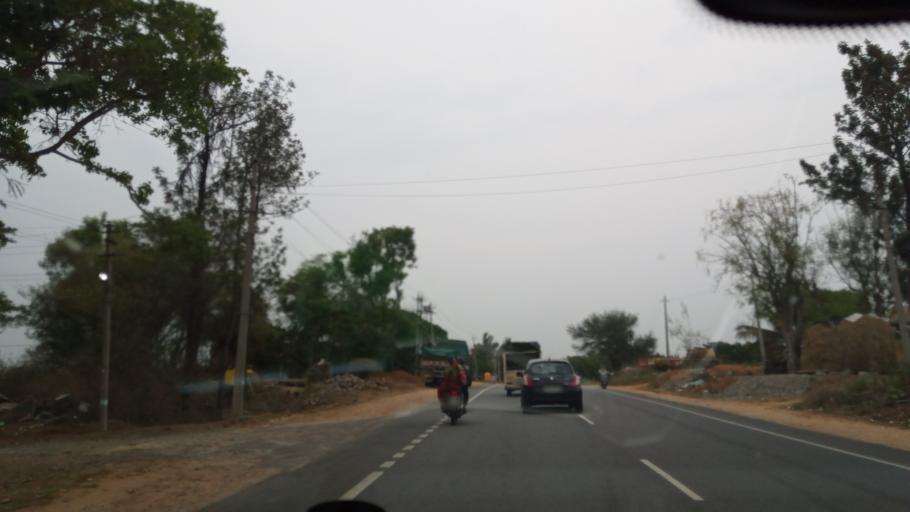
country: IN
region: Karnataka
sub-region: Mandya
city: Belluru
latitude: 12.9366
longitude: 76.7503
